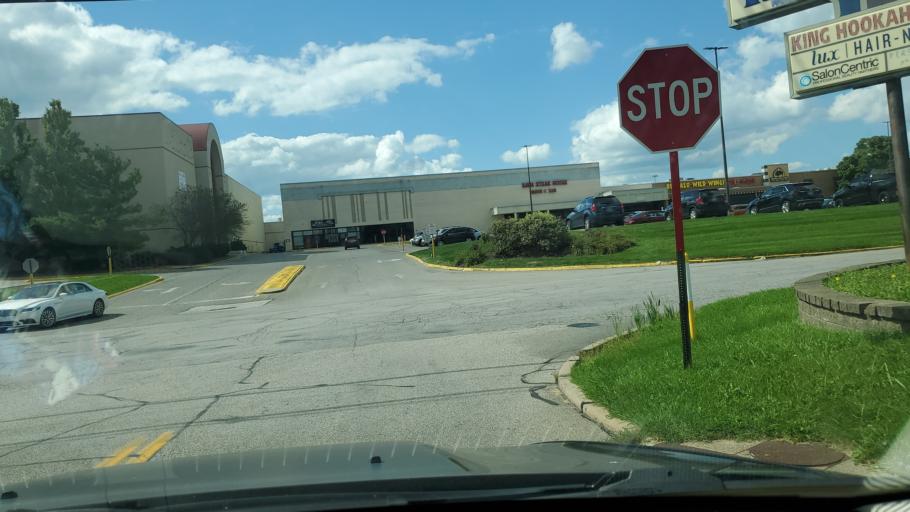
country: US
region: Ohio
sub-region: Mahoning County
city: Boardman
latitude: 41.0210
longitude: -80.6562
